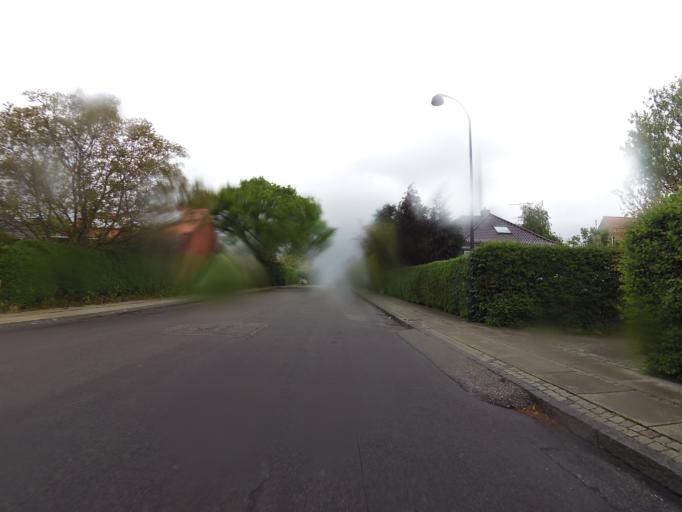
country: DK
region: Capital Region
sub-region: Frederiksberg Kommune
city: Frederiksberg
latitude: 55.7295
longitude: 12.5419
